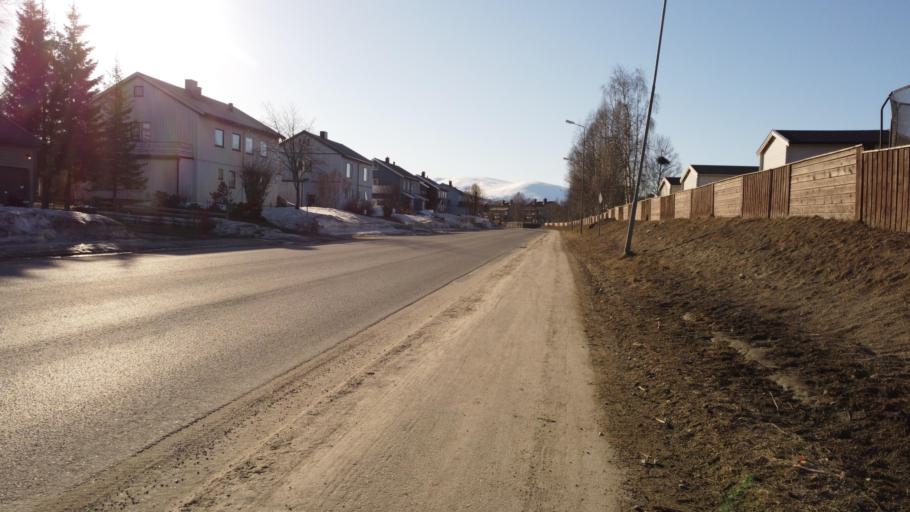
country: NO
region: Nordland
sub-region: Rana
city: Mo i Rana
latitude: 66.3189
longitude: 14.1912
